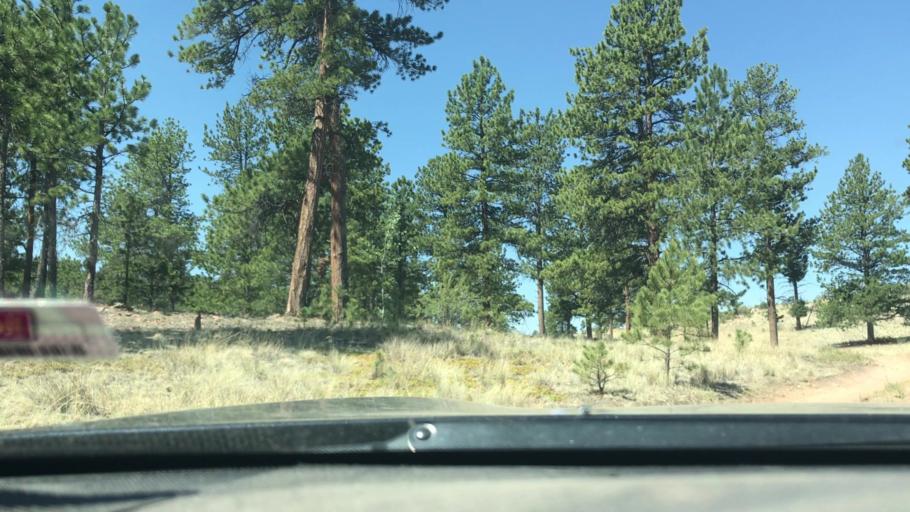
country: US
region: Colorado
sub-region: Teller County
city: Woodland Park
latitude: 38.9962
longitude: -105.3418
